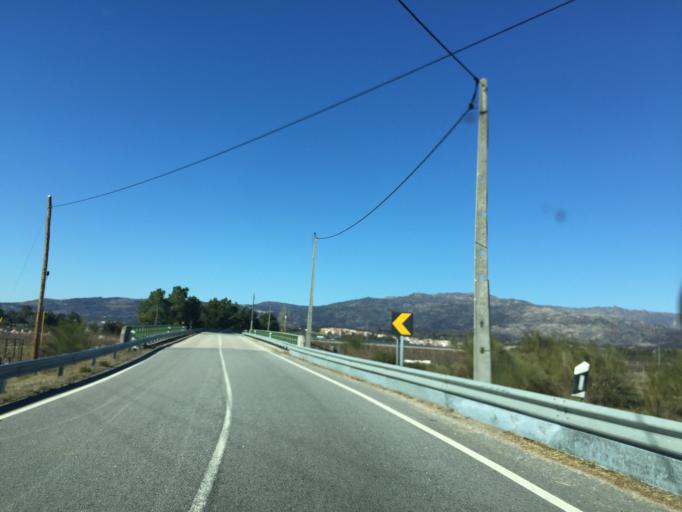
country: PT
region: Guarda
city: Alcains
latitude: 40.0168
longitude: -7.4656
